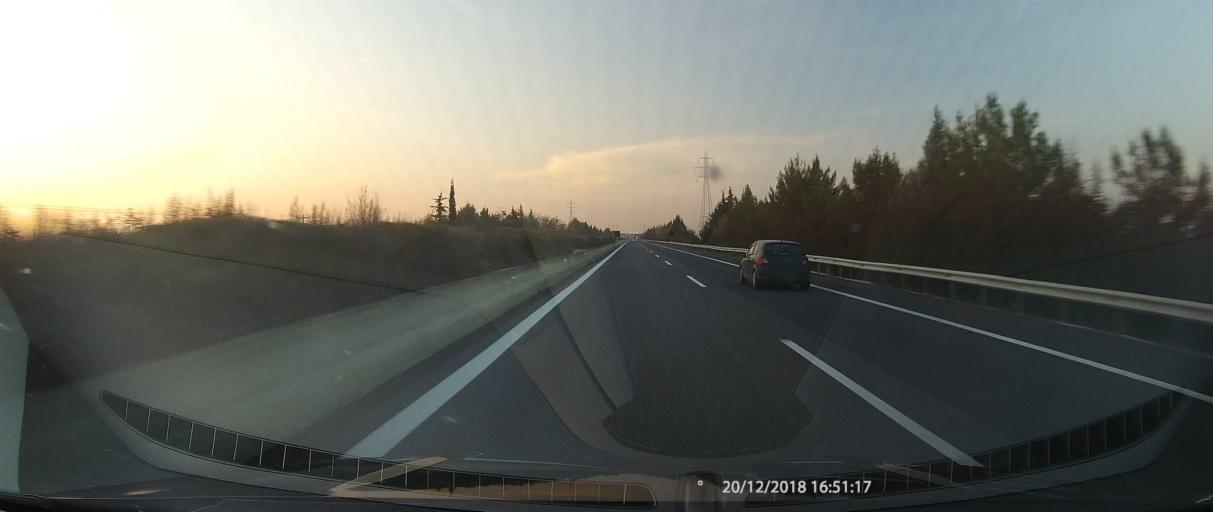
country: GR
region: Thessaly
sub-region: Nomos Larisis
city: Chalki
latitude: 39.5140
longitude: 22.5699
